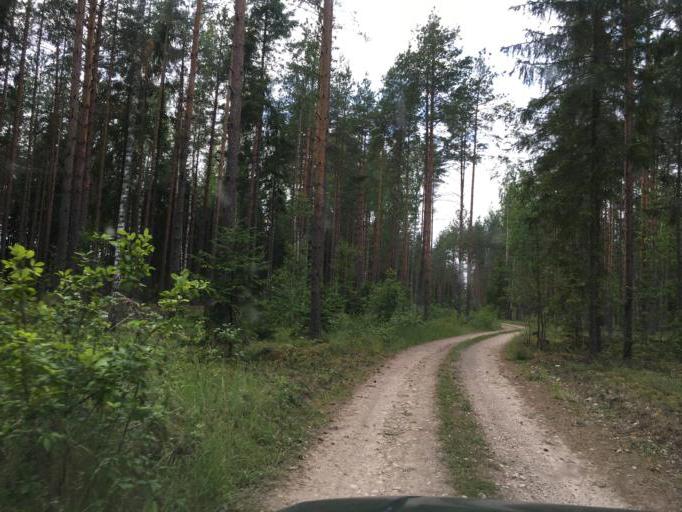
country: LV
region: Vilanu
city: Vilani
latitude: 56.7182
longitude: 26.9439
